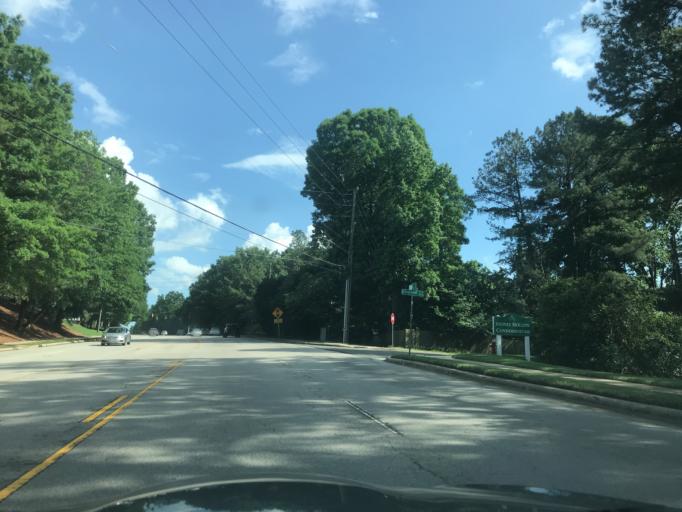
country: US
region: North Carolina
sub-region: Wake County
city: West Raleigh
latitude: 35.8757
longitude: -78.6450
